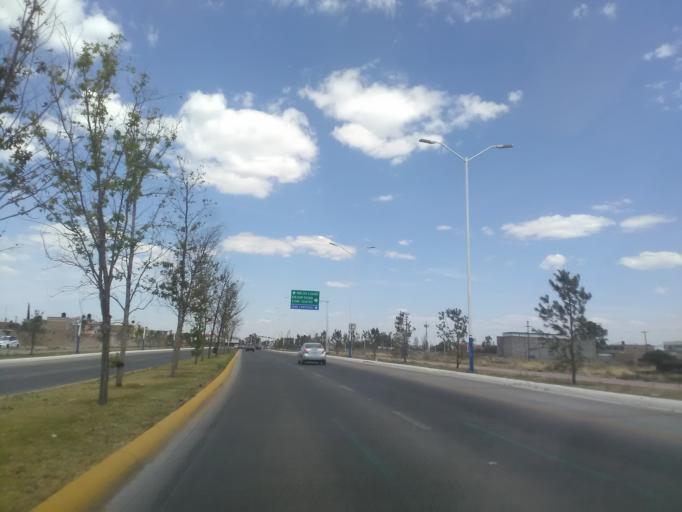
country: MX
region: Durango
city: Victoria de Durango
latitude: 24.0370
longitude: -104.6631
